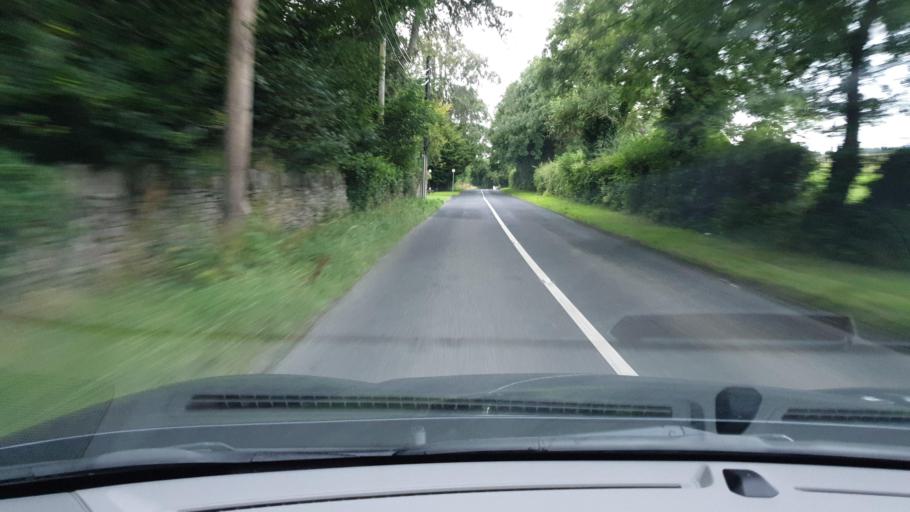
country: IE
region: Leinster
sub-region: South Dublin
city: Rathcoole
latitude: 53.2588
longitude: -6.4978
